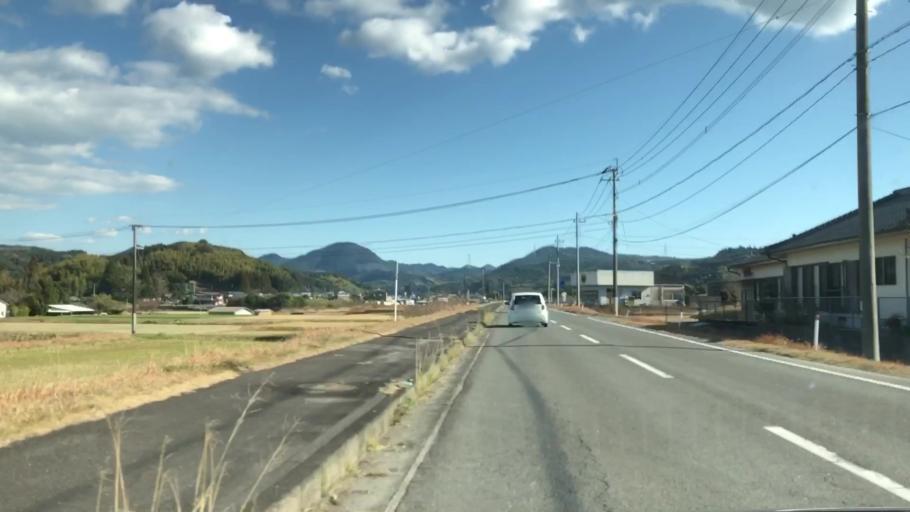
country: JP
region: Kagoshima
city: Satsumasendai
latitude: 31.7969
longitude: 130.4358
